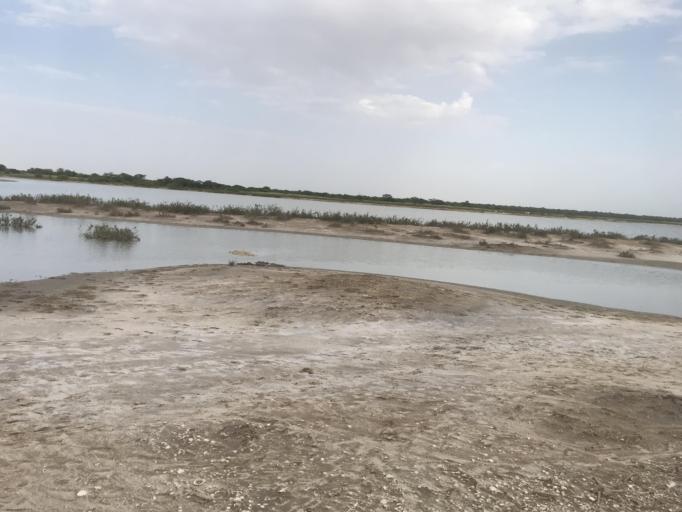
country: SN
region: Saint-Louis
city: Saint-Louis
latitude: 15.9295
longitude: -16.4641
